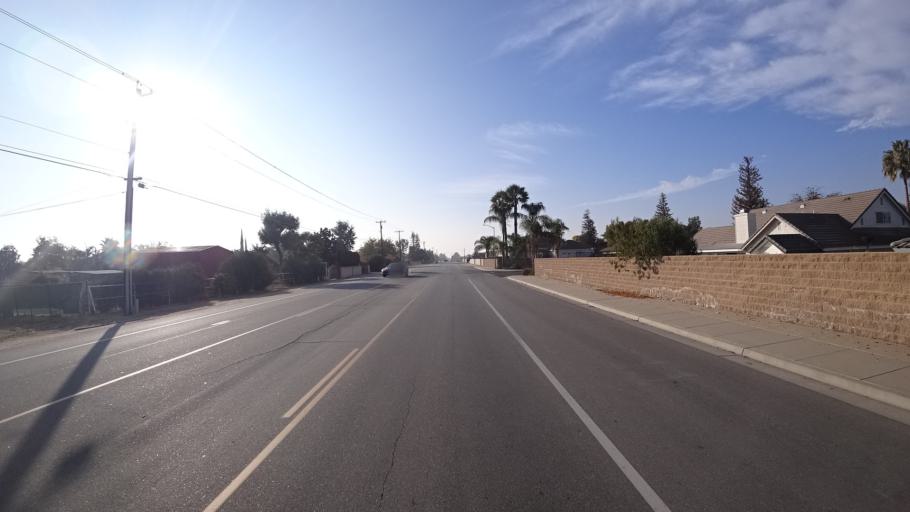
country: US
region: California
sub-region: Kern County
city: Rosedale
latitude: 35.3729
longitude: -119.1634
